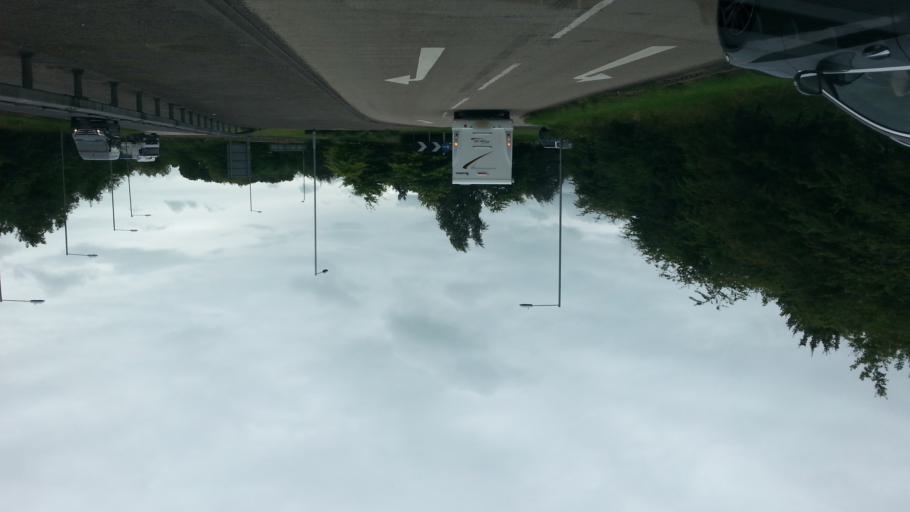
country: GB
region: England
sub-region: Wiltshire
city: Melksham
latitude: 51.3639
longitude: -2.1385
